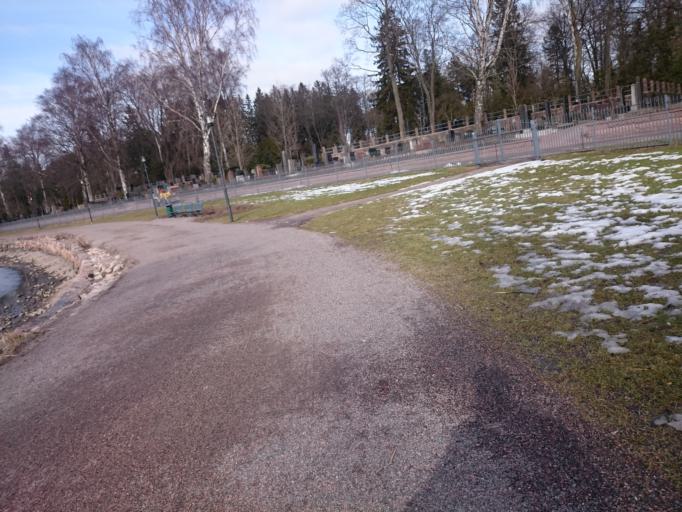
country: FI
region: Uusimaa
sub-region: Helsinki
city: Helsinki
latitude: 60.1693
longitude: 24.9162
